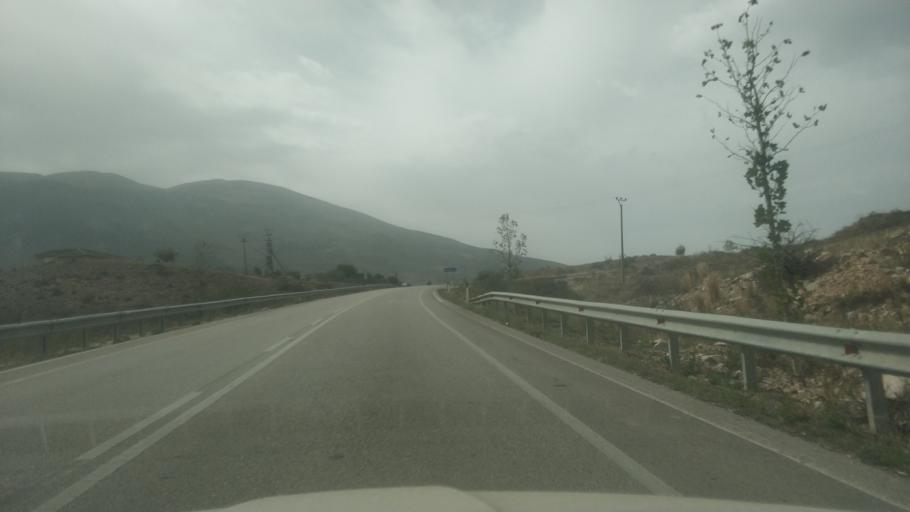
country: AL
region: Gjirokaster
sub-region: Rrethi i Tepelenes
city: Memaliaj
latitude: 40.3557
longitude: 19.9408
